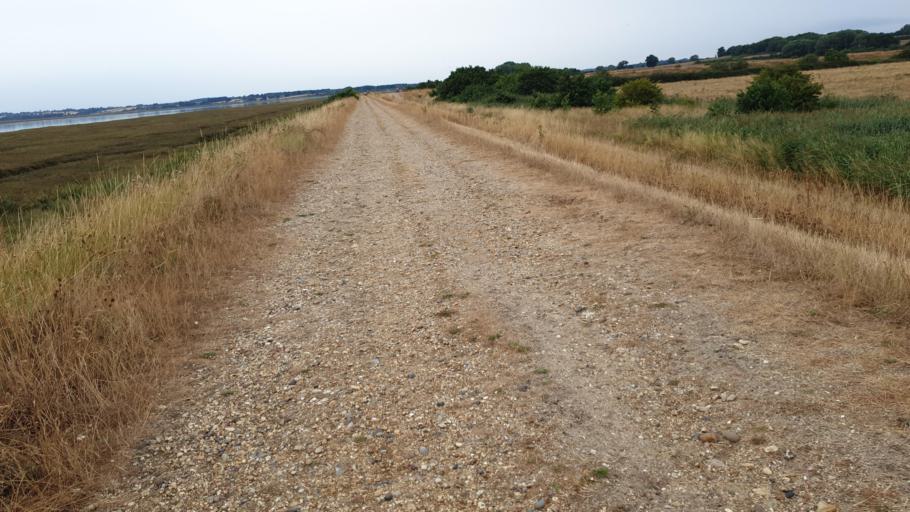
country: GB
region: England
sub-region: Essex
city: Brightlingsea
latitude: 51.8143
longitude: 0.9990
